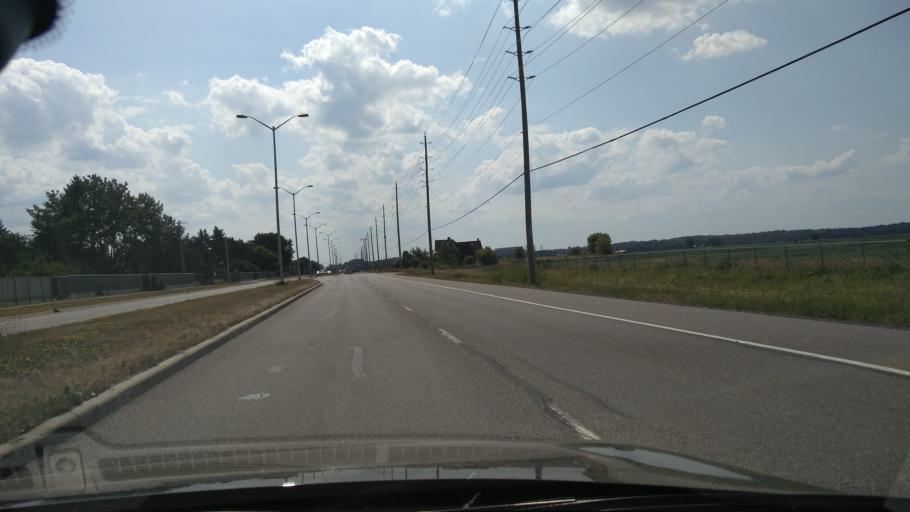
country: CA
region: Ontario
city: Bells Corners
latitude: 45.2925
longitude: -75.7466
